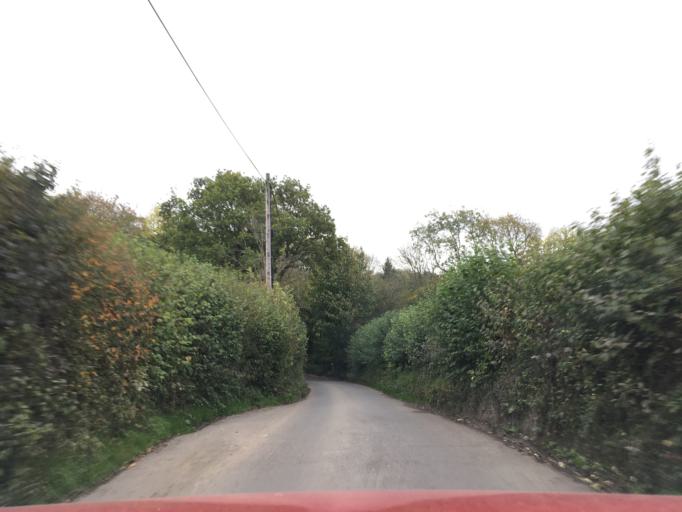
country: GB
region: England
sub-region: South Gloucestershire
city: Wickwar
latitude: 51.5983
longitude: -2.3768
